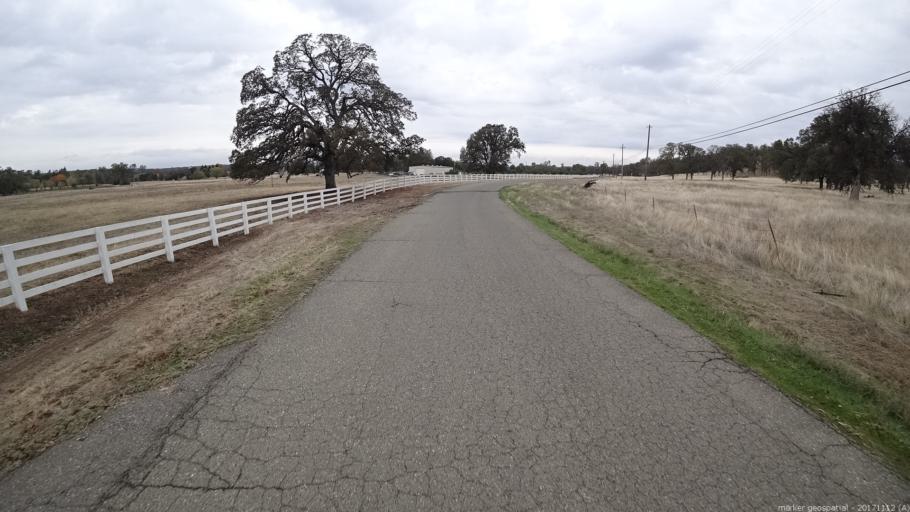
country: US
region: California
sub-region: Shasta County
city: Palo Cedro
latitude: 40.5295
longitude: -122.2256
